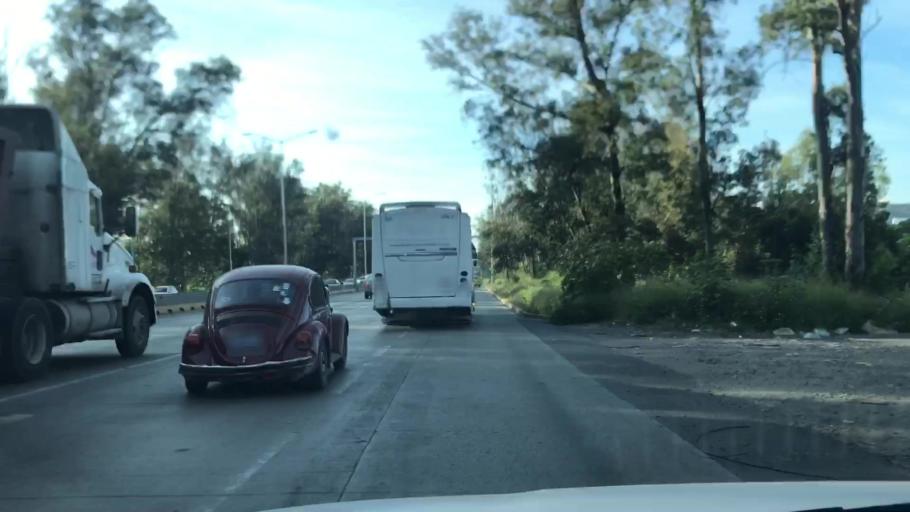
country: MX
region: Jalisco
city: Zapopan2
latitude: 20.6864
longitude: -103.4554
